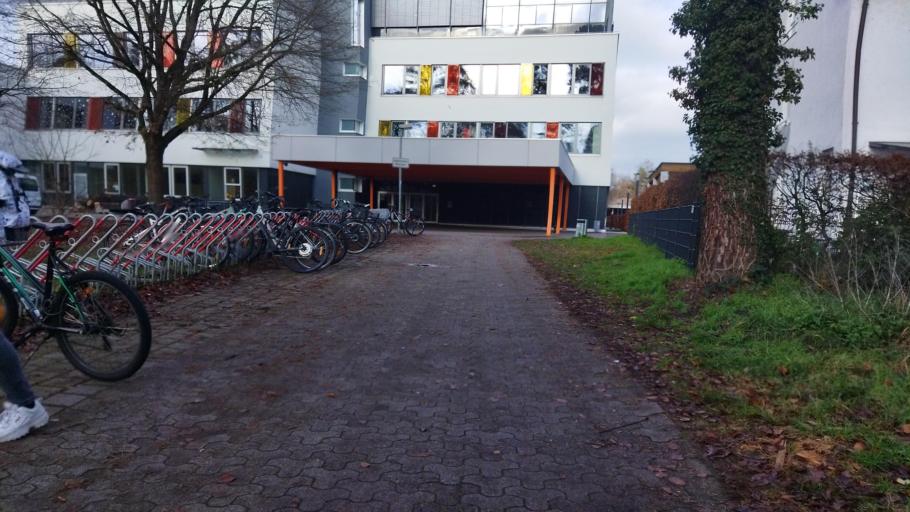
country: DE
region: Baden-Wuerttemberg
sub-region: Karlsruhe Region
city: Walldorf
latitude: 49.3133
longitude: 8.6360
